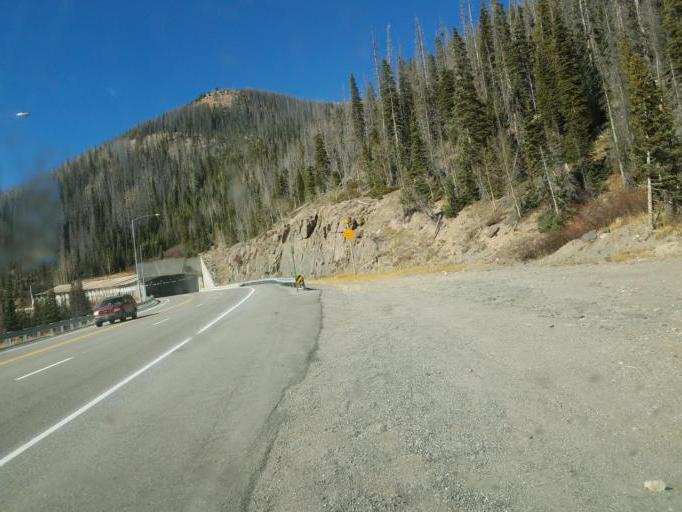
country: US
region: Colorado
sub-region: Archuleta County
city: Pagosa Springs
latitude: 37.4794
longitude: -106.7775
